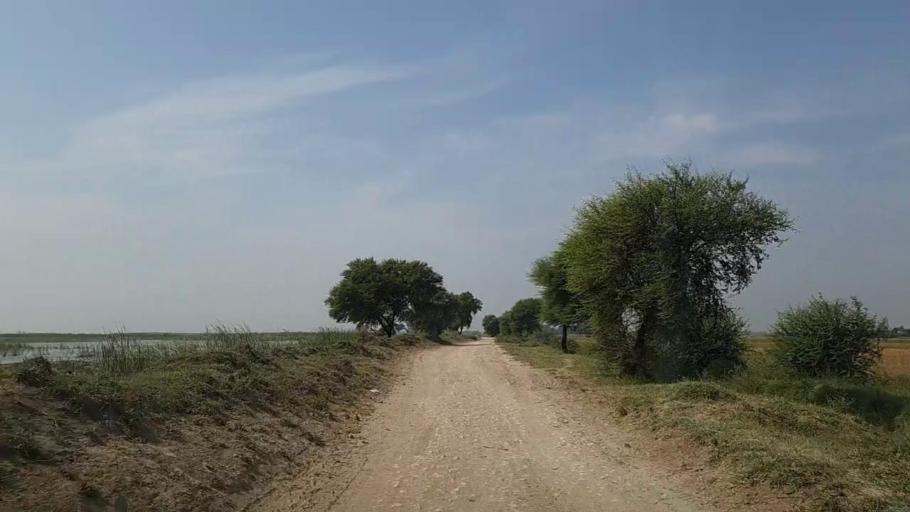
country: PK
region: Sindh
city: Mirpur Batoro
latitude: 24.6113
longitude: 68.2305
